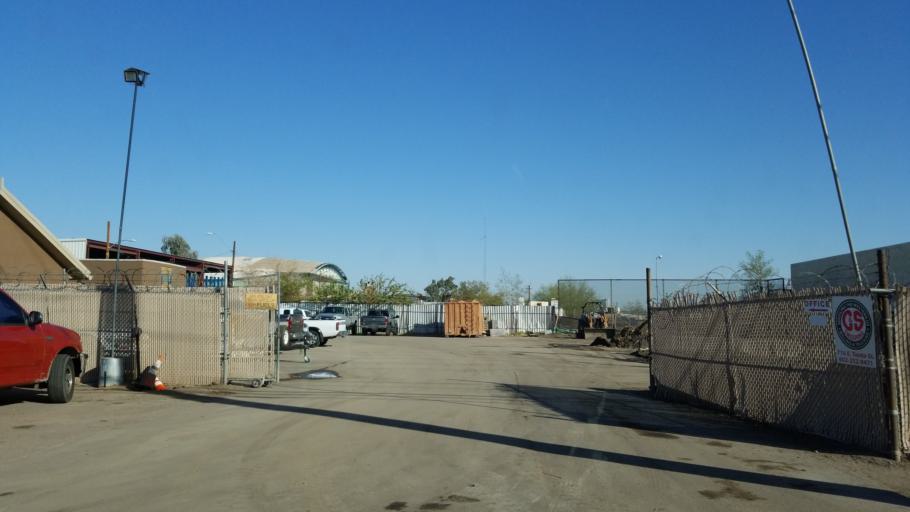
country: US
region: Arizona
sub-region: Maricopa County
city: Phoenix
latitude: 33.4379
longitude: -112.0632
